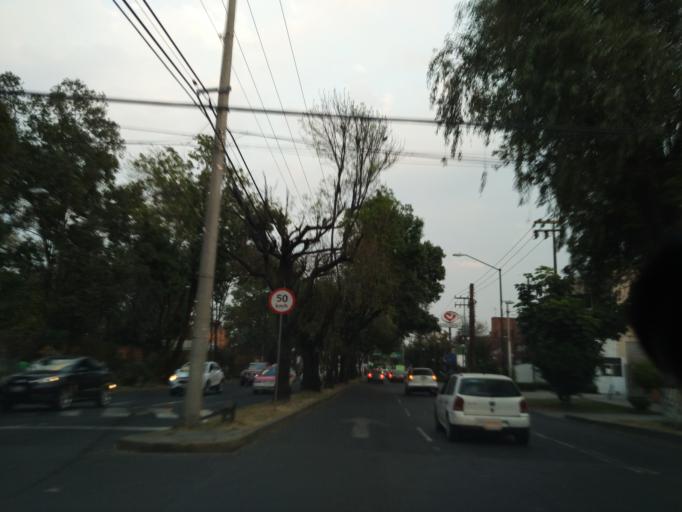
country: MX
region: Mexico City
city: Xochimilco
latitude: 19.3011
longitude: -99.1156
